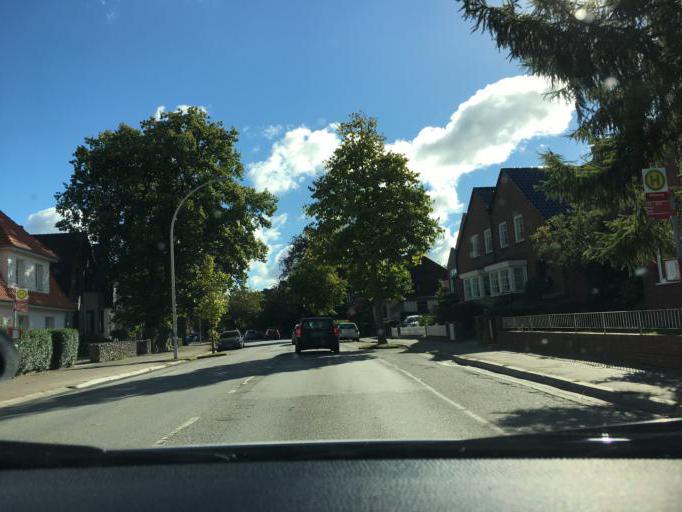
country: DE
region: Schleswig-Holstein
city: Kronshagen
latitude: 54.3305
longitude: 10.0886
